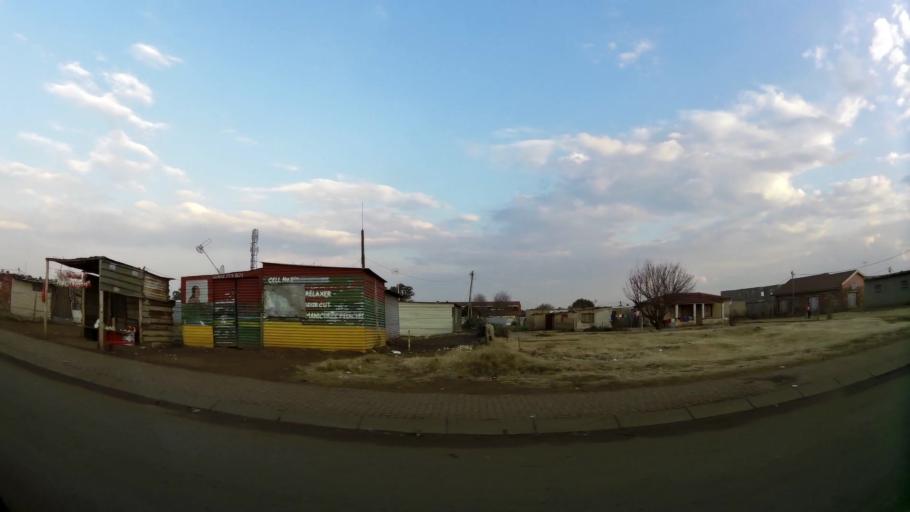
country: ZA
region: Gauteng
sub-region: City of Johannesburg Metropolitan Municipality
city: Orange Farm
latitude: -26.5370
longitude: 27.8332
